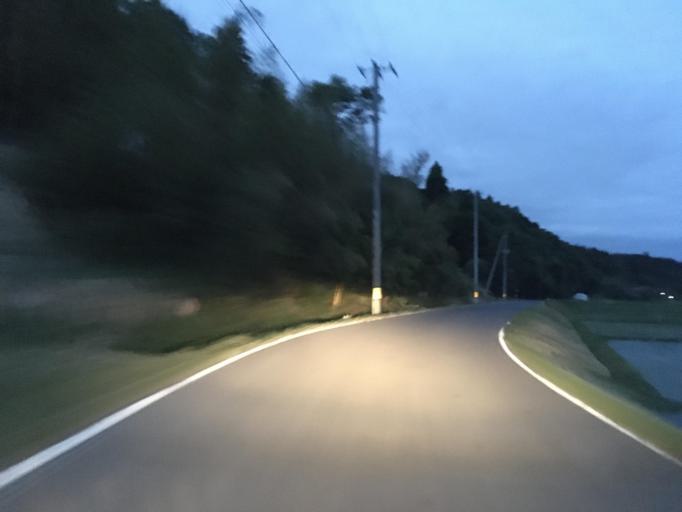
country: JP
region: Miyagi
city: Furukawa
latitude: 38.7866
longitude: 140.9442
